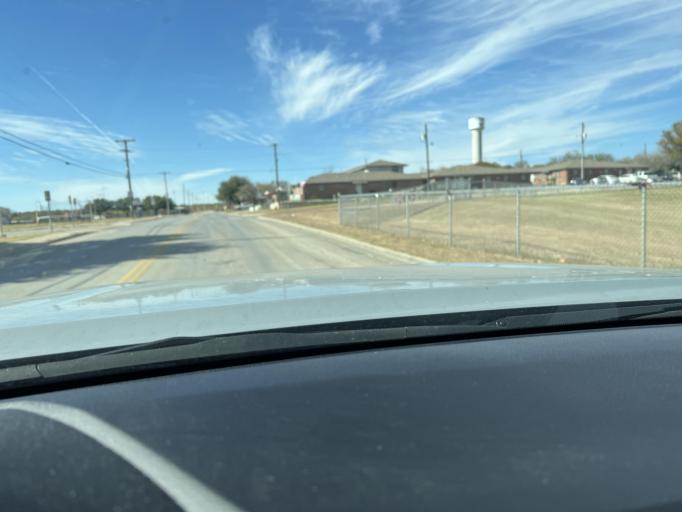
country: US
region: Texas
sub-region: Eastland County
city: Eastland
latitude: 32.3955
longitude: -98.8287
